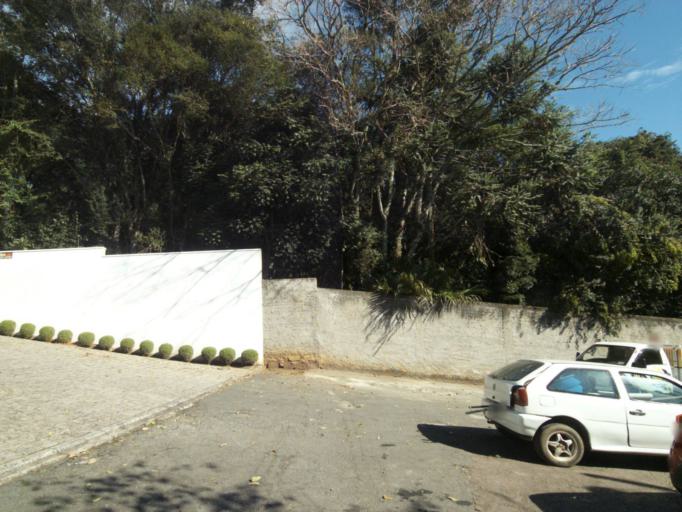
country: BR
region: Parana
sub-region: Curitiba
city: Curitiba
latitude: -25.4058
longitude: -49.2734
